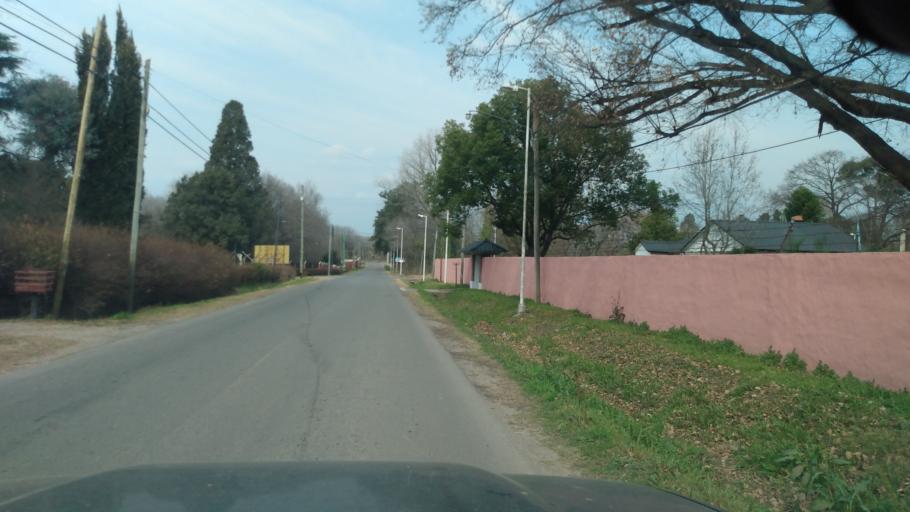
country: AR
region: Buenos Aires
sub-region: Partido de Lujan
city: Lujan
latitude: -34.5572
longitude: -59.1242
